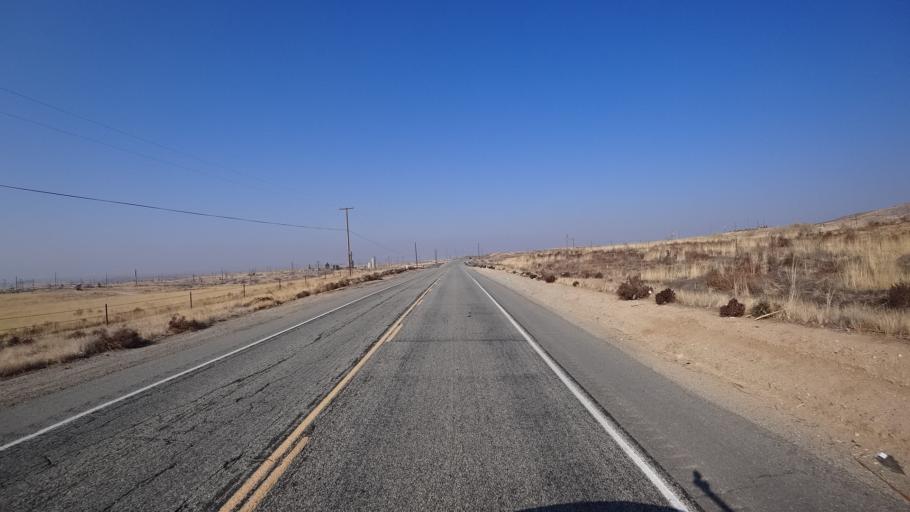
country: US
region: California
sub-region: Kern County
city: Lamont
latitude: 35.3764
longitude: -118.8460
